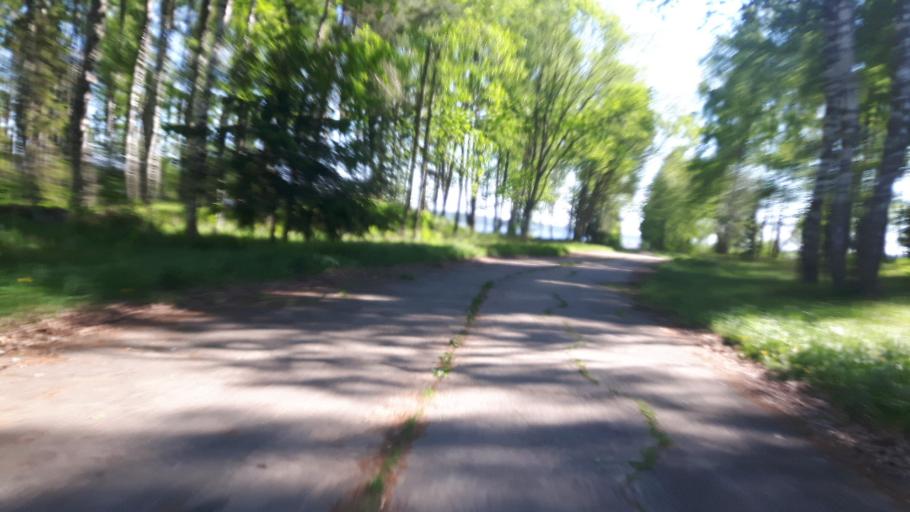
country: RU
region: Leningrad
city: Sista-Palkino
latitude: 59.7624
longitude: 28.7401
